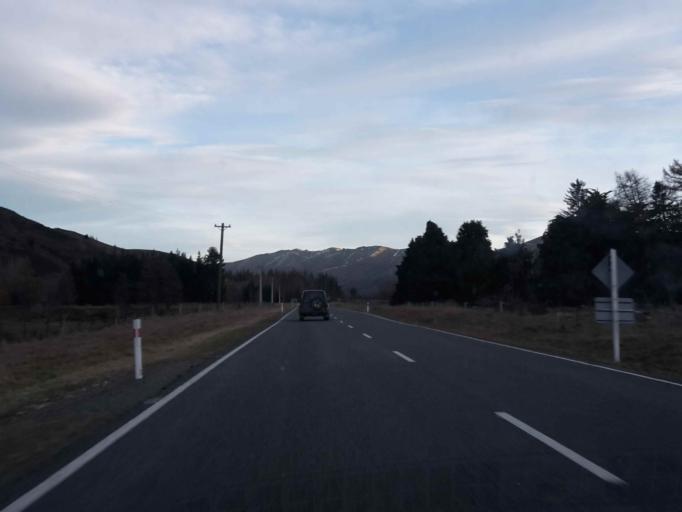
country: NZ
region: Canterbury
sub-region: Timaru District
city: Pleasant Point
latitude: -44.0758
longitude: 170.6660
